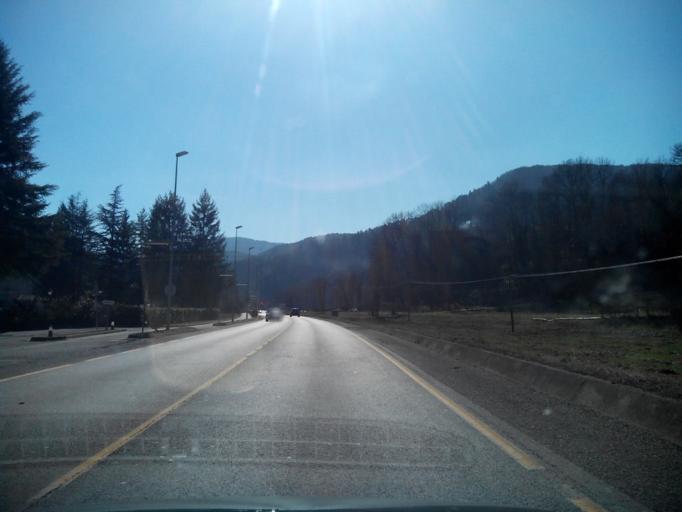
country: ES
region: Catalonia
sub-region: Provincia de Girona
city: Ripoll
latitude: 42.1826
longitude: 2.1954
